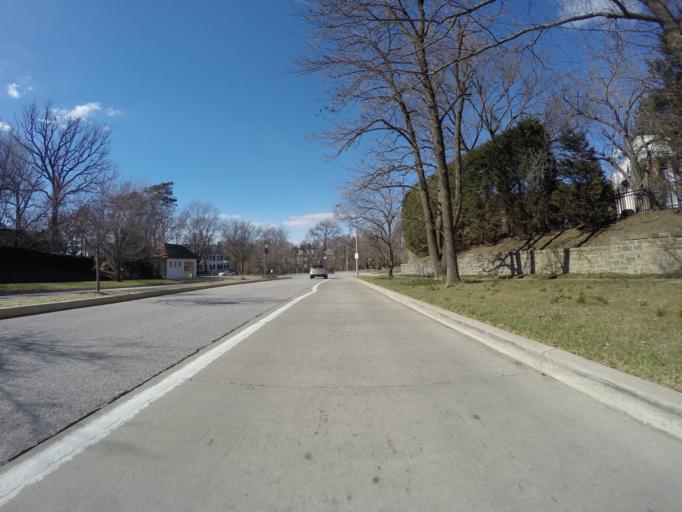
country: US
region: Maryland
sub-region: City of Baltimore
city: Baltimore
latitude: 39.3421
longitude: -76.6202
